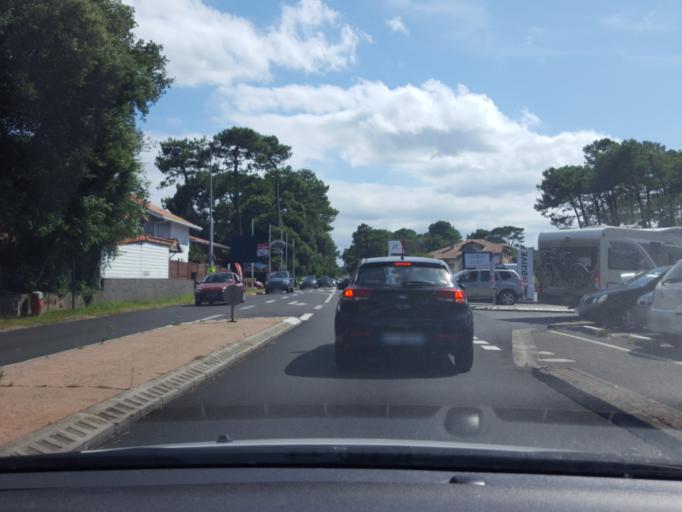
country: FR
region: Aquitaine
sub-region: Departement des Landes
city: Capbreton
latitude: 43.6387
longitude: -1.4259
